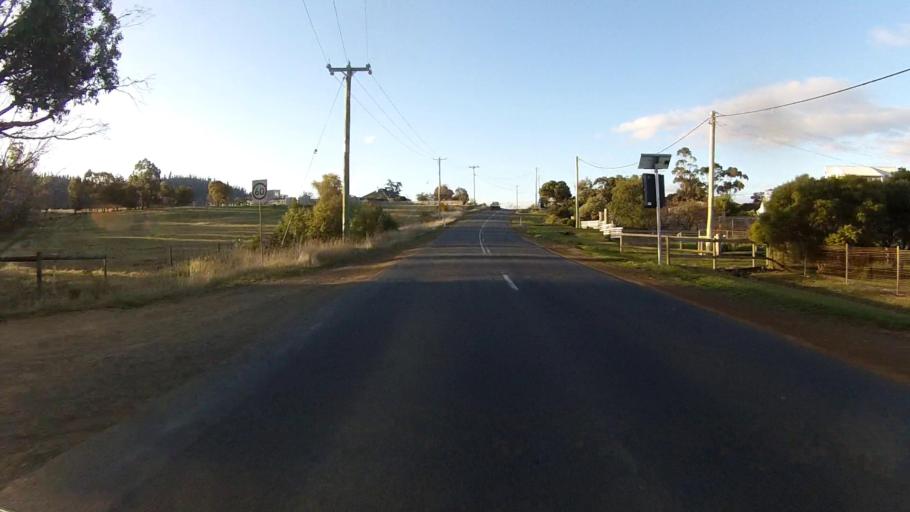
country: AU
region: Tasmania
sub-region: Sorell
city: Sorell
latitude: -42.8850
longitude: 147.8136
